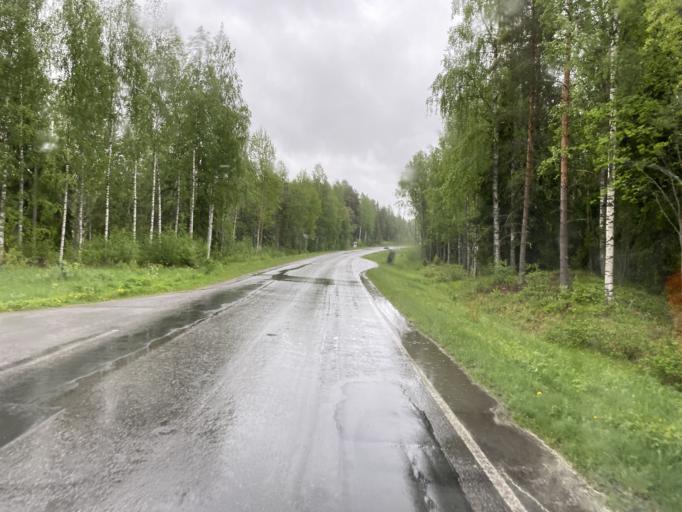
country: FI
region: Pirkanmaa
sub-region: Etelae-Pirkanmaa
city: Urjala
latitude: 61.0404
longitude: 23.4427
